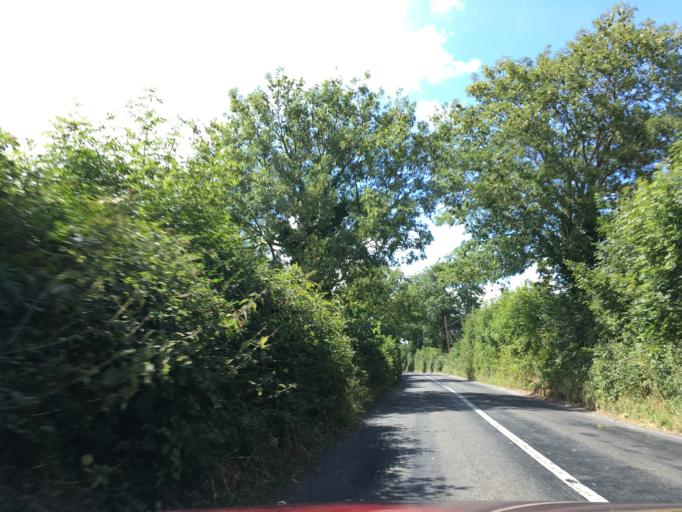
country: IE
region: Munster
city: Cahir
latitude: 52.3430
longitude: -7.9500
